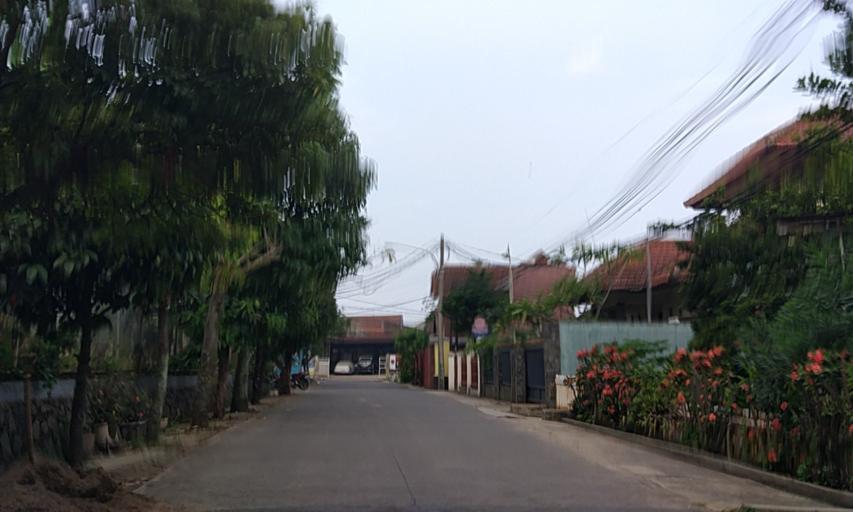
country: ID
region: West Java
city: Bandung
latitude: -6.9073
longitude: 107.6767
